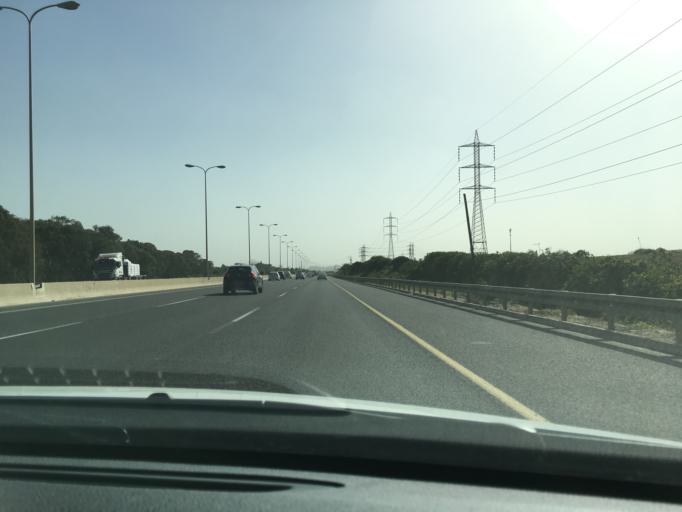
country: IL
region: Central District
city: Hod HaSharon
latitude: 32.1527
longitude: 34.8726
